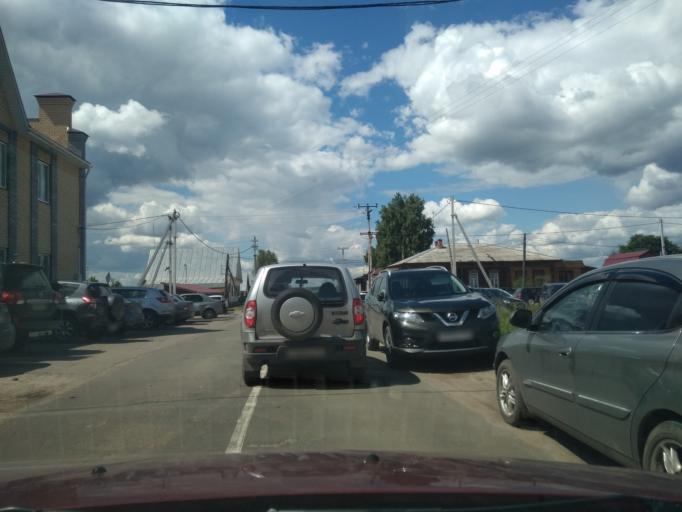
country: RU
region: Vladimir
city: Melenki
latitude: 55.3412
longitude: 41.6344
